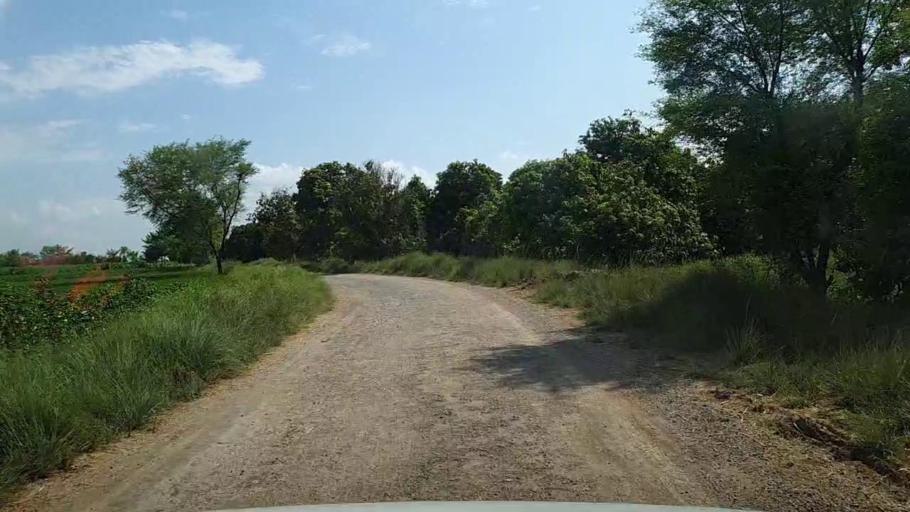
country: PK
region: Sindh
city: Bhiria
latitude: 26.9079
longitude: 68.2255
